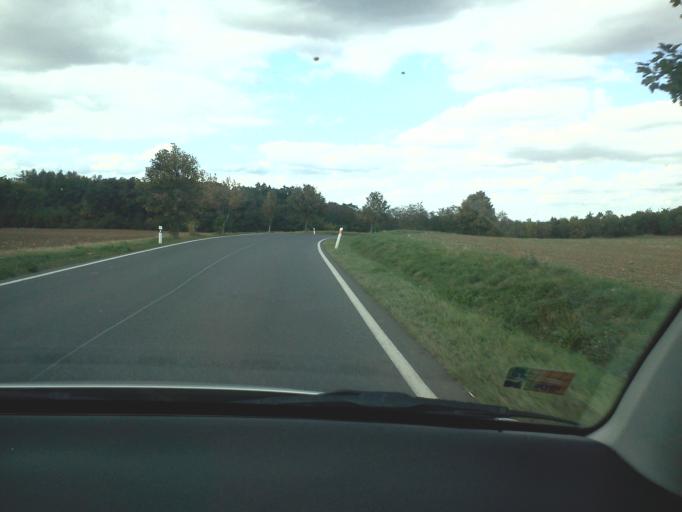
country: CZ
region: Central Bohemia
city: Cesky Brod
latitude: 50.0998
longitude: 14.8613
